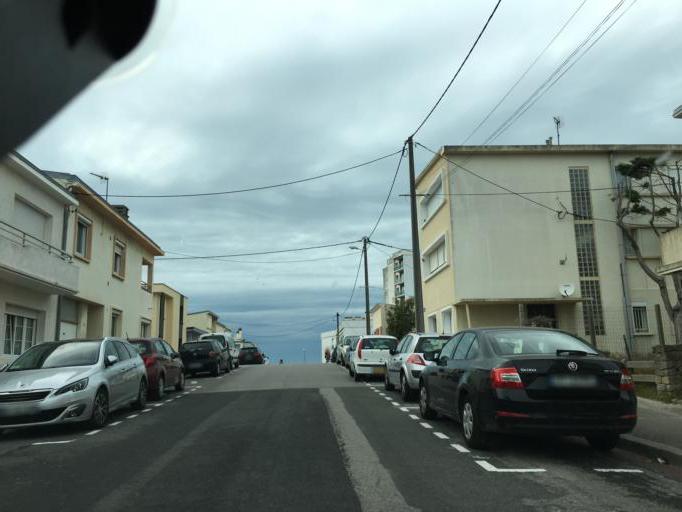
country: FR
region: Nord-Pas-de-Calais
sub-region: Departement du Pas-de-Calais
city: Berck-Plage
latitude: 50.4031
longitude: 1.5604
